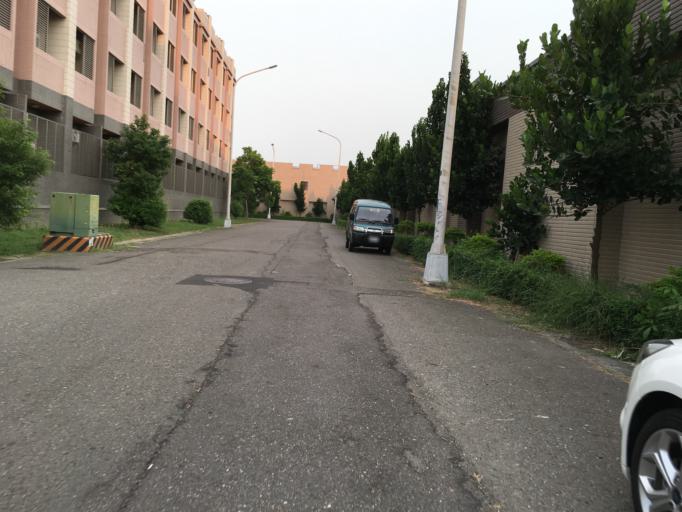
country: TW
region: Taiwan
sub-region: Chiayi
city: Taibao
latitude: 23.4547
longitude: 120.2888
